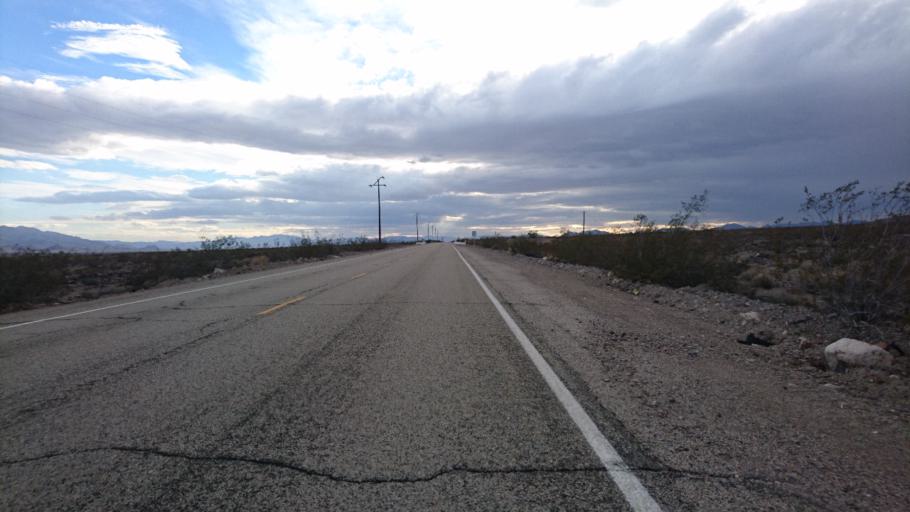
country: US
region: California
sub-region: San Bernardino County
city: Needles
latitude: 34.6607
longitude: -115.3540
